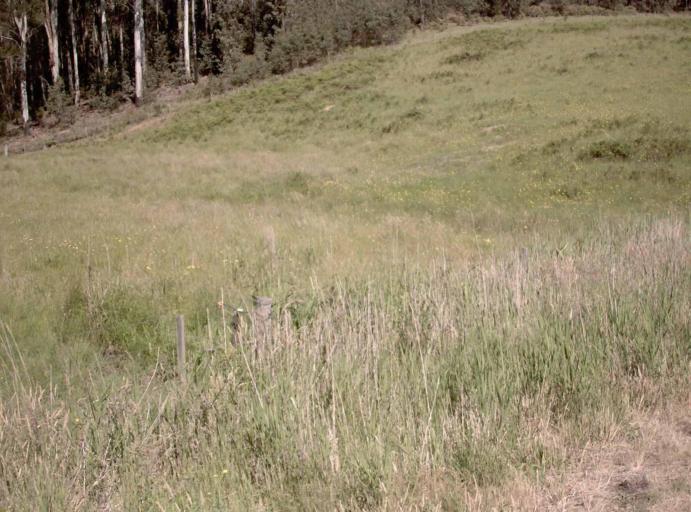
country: AU
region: New South Wales
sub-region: Bombala
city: Bombala
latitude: -37.1985
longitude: 148.7260
